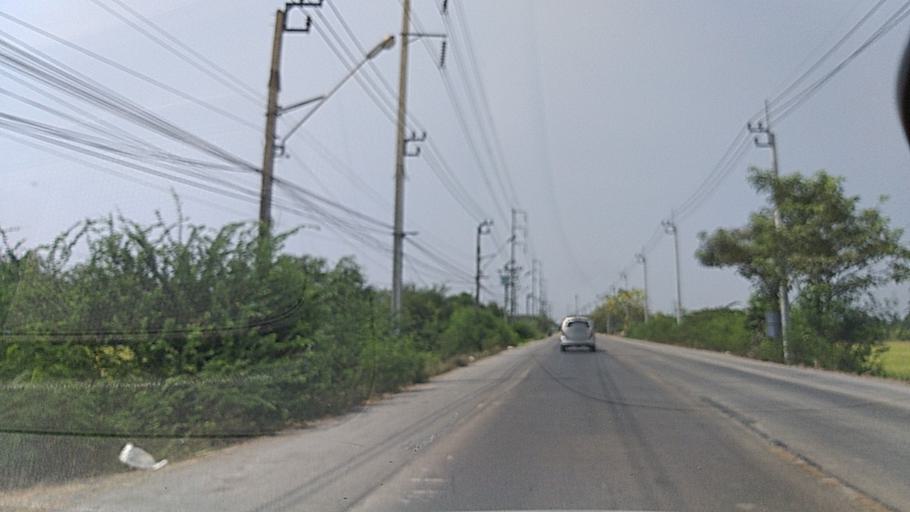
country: TH
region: Nonthaburi
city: Sai Noi
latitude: 13.9506
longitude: 100.3128
